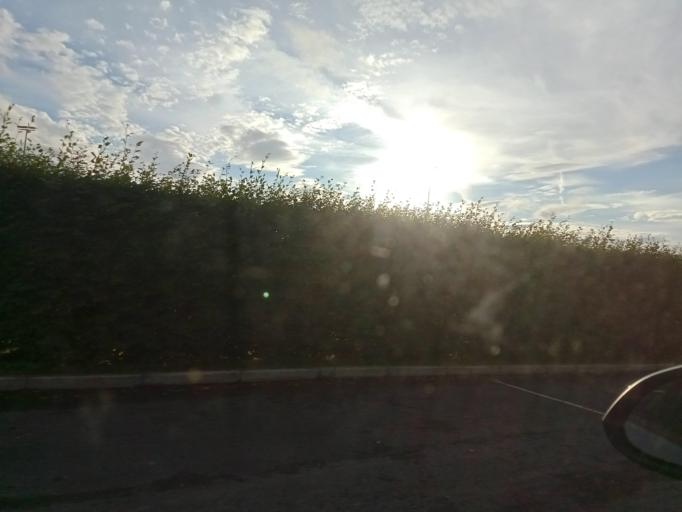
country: IE
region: Leinster
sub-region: Laois
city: Stradbally
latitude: 53.0067
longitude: -7.2159
